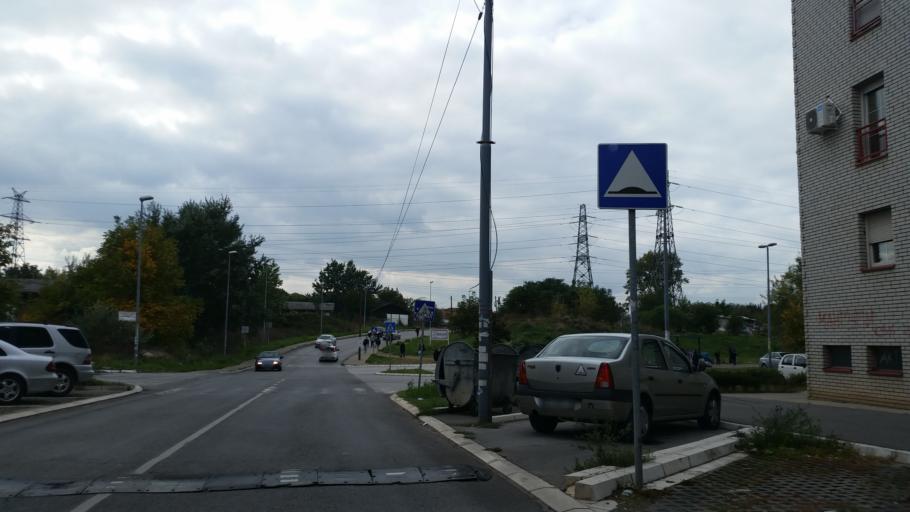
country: RS
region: Central Serbia
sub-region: Belgrade
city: Zemun
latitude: 44.8081
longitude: 20.3638
